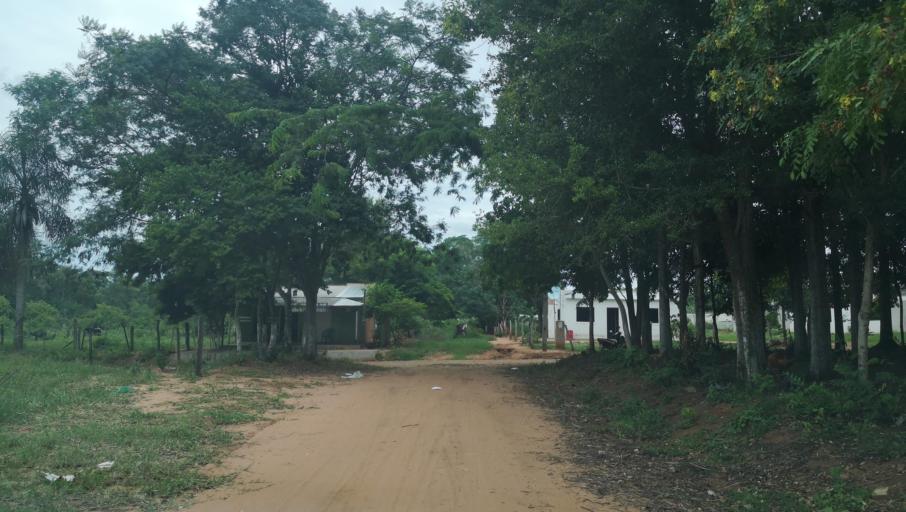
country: PY
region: San Pedro
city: Capiibary
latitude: -24.7390
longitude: -56.0227
